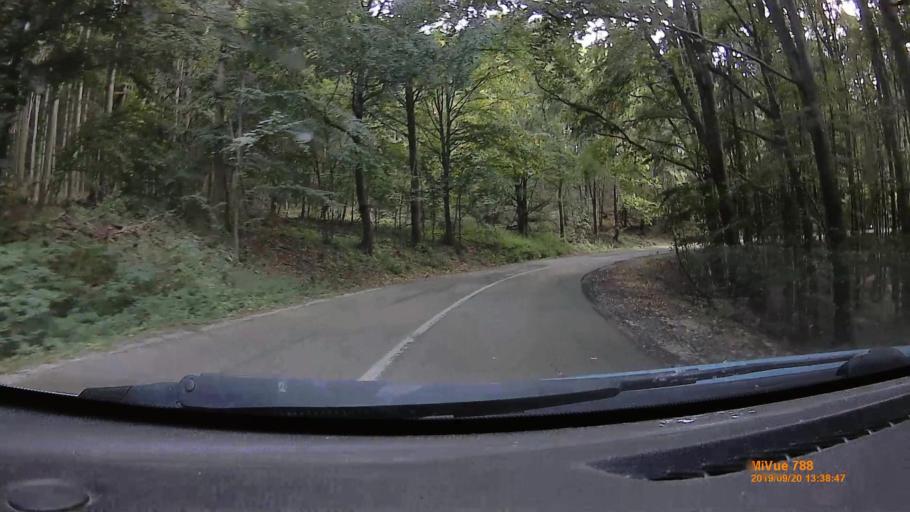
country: HU
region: Heves
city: Szilvasvarad
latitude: 48.0605
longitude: 20.5280
